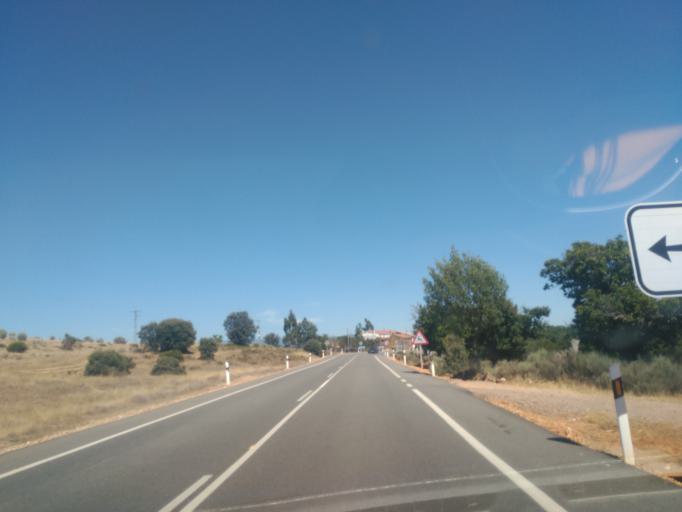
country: ES
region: Castille and Leon
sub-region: Provincia de Zamora
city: Villardeciervos
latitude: 41.9732
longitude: -6.2308
